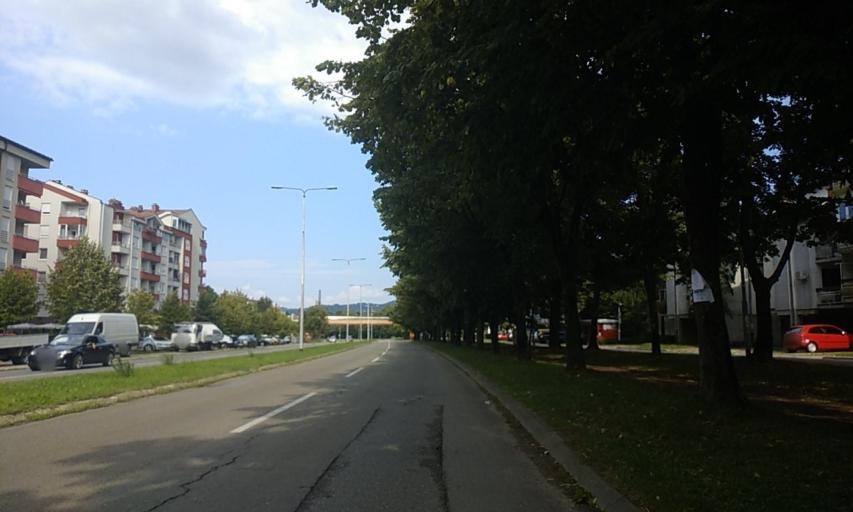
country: BA
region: Republika Srpska
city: Starcevica
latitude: 44.7631
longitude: 17.2047
